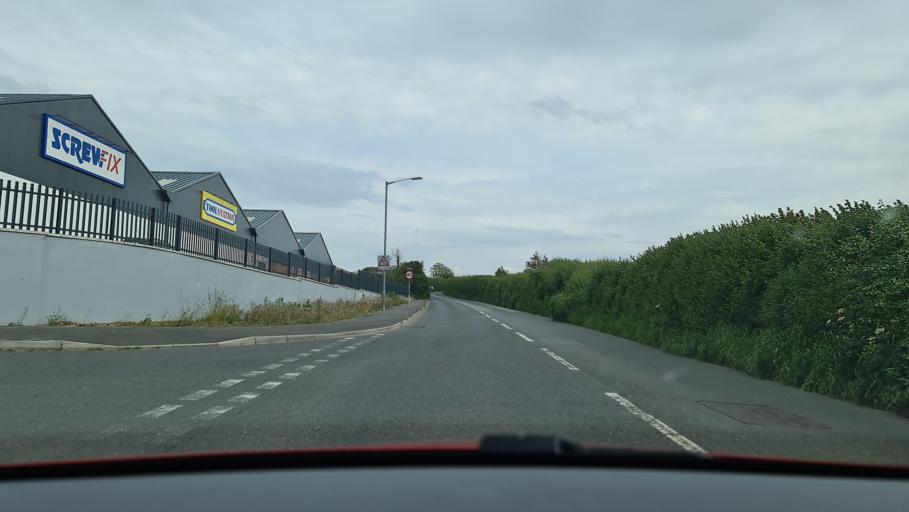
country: GB
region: England
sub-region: Cornwall
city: Bude
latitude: 50.8198
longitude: -4.5333
